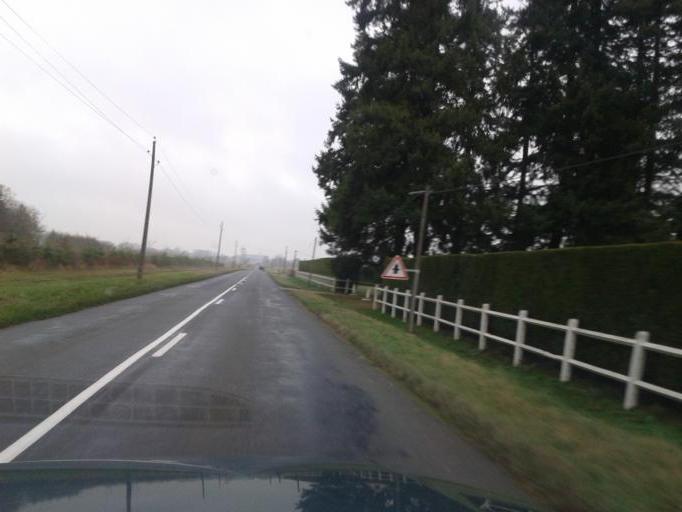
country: FR
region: Centre
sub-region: Departement du Loiret
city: Beaugency
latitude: 47.7642
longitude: 1.6428
